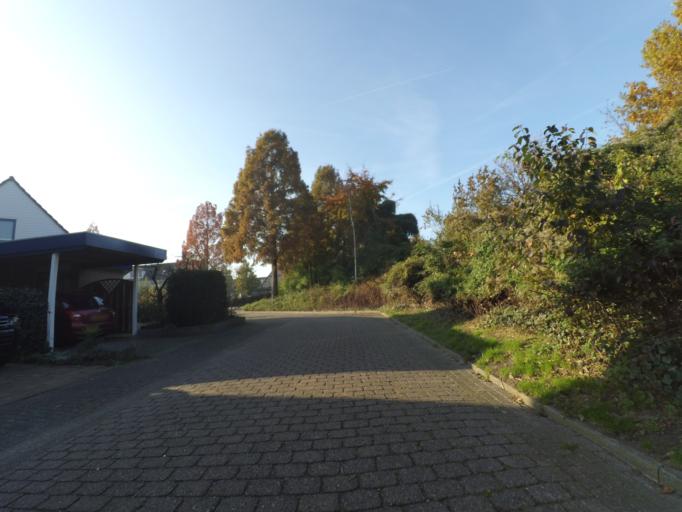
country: NL
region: Utrecht
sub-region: Gemeente Leusden
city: Leusden
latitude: 52.1418
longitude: 5.4338
